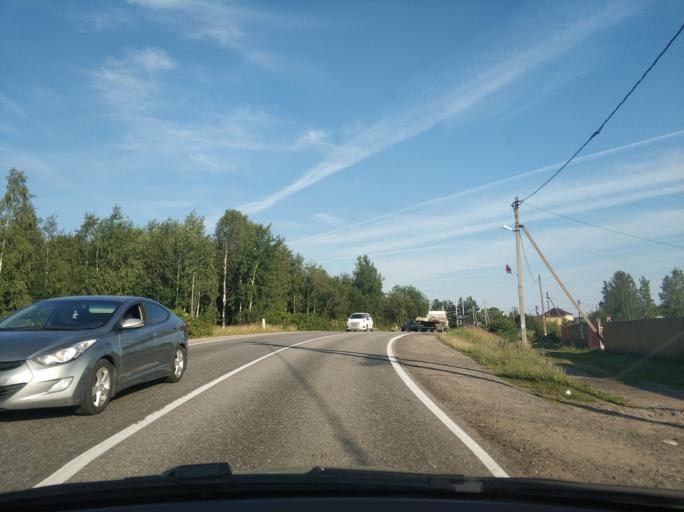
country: RU
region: Leningrad
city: Borisova Griva
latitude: 60.0910
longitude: 31.0171
